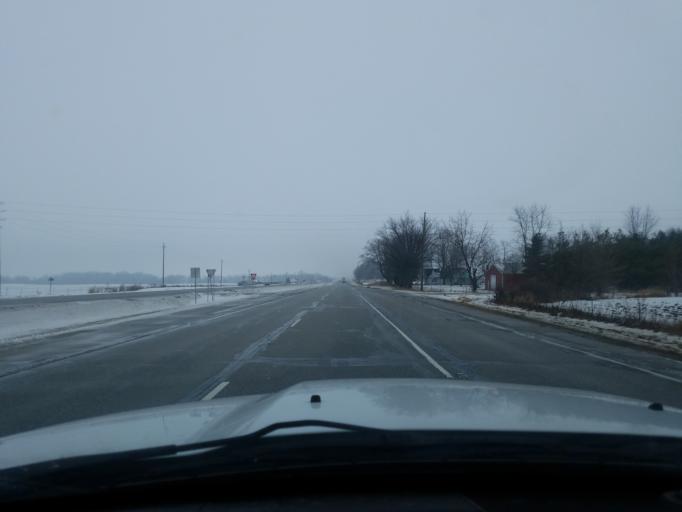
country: US
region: Indiana
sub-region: Miami County
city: Grissom Air Force Base
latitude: 40.5987
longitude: -86.1275
